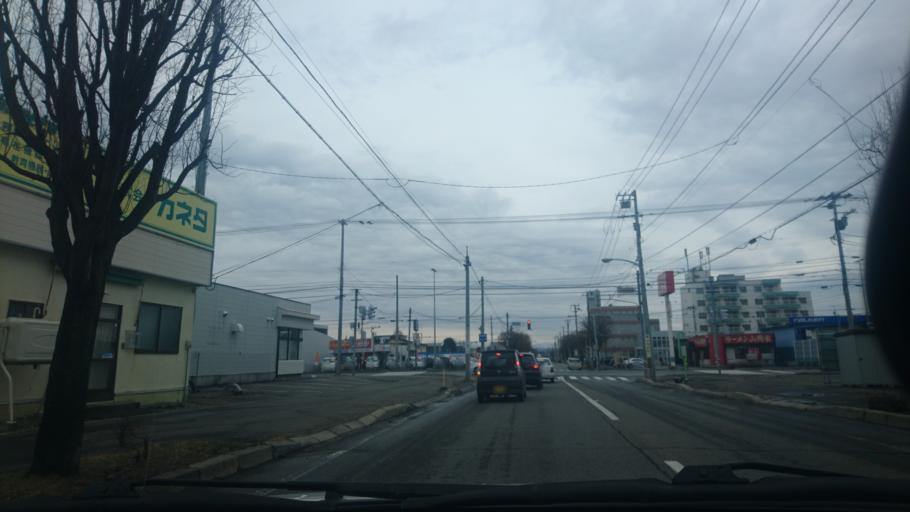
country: JP
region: Hokkaido
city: Obihiro
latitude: 42.9307
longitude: 143.1930
